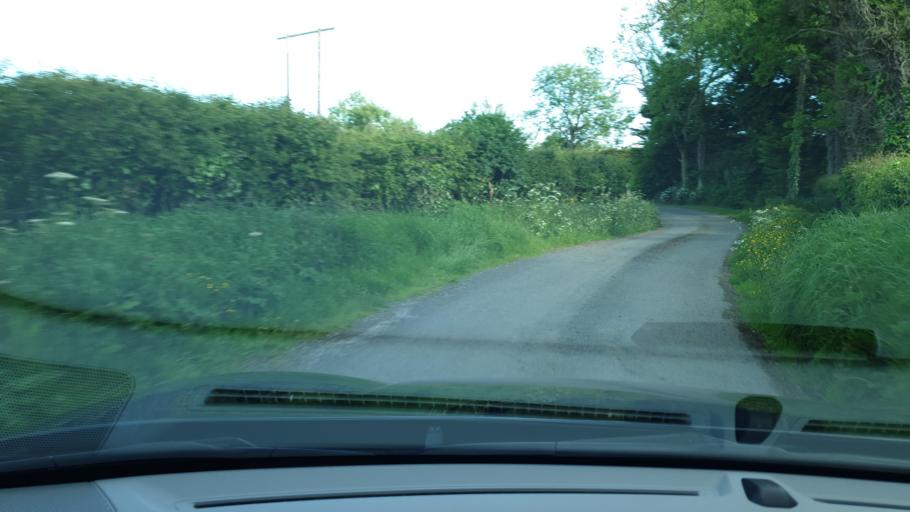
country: IE
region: Leinster
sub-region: An Mhi
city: Ratoath
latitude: 53.5595
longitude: -6.4366
